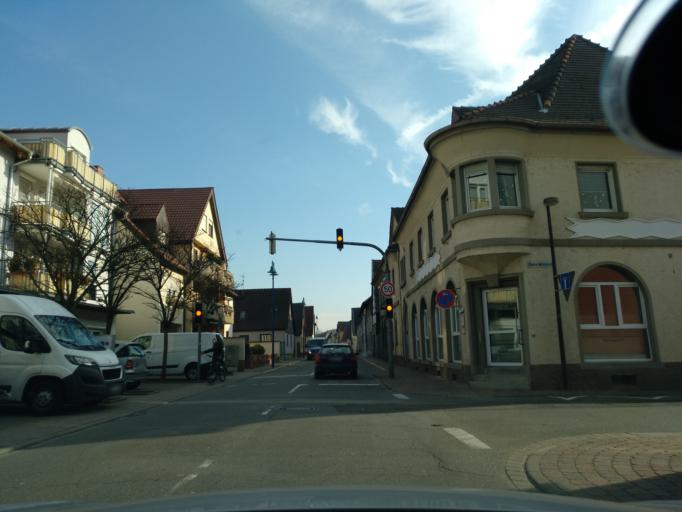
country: DE
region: Baden-Wuerttemberg
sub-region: Karlsruhe Region
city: Hockenheim
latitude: 49.3159
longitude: 8.5501
